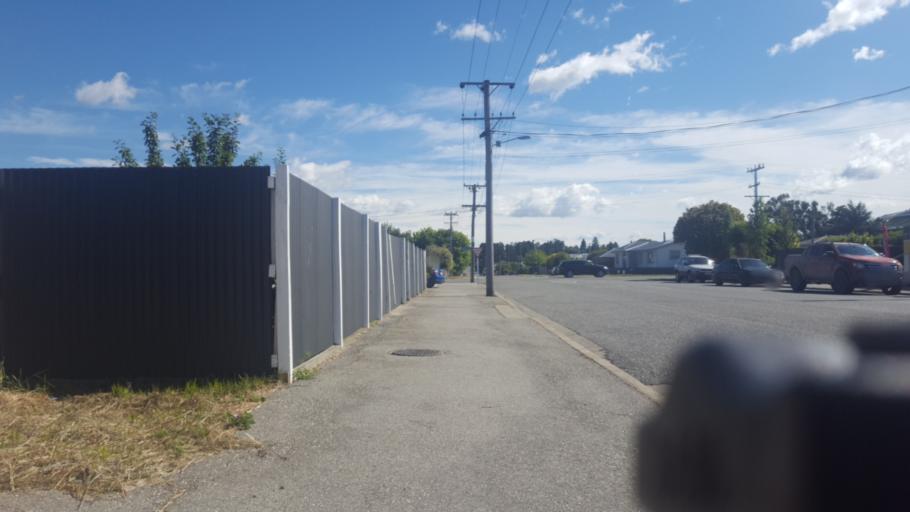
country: NZ
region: Otago
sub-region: Queenstown-Lakes District
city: Wanaka
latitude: -45.0486
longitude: 169.2054
